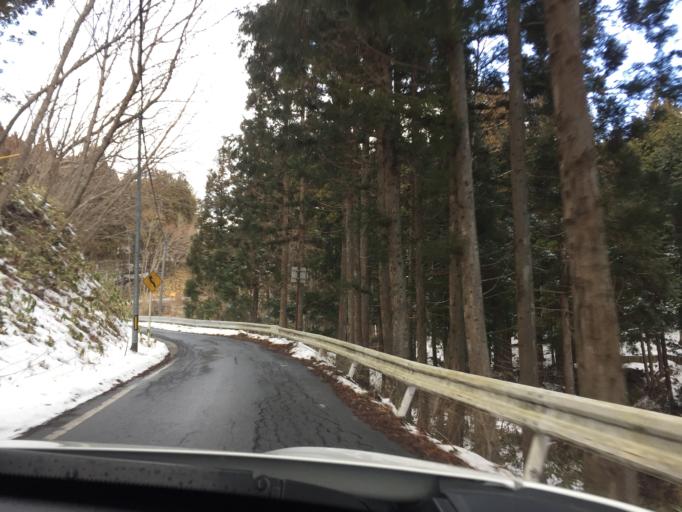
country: JP
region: Fukushima
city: Funehikimachi-funehiki
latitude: 37.2818
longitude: 140.7233
